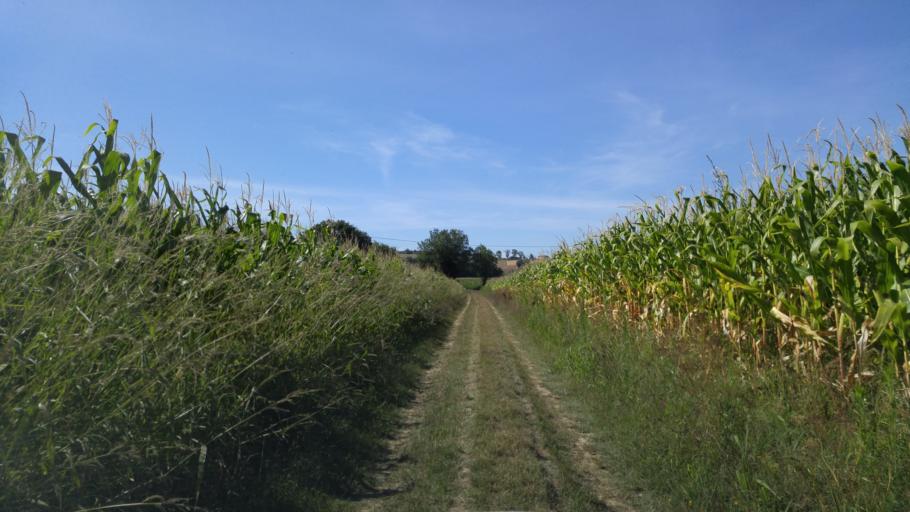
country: IT
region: The Marches
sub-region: Provincia di Pesaro e Urbino
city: Cuccurano
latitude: 43.7836
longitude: 12.9560
